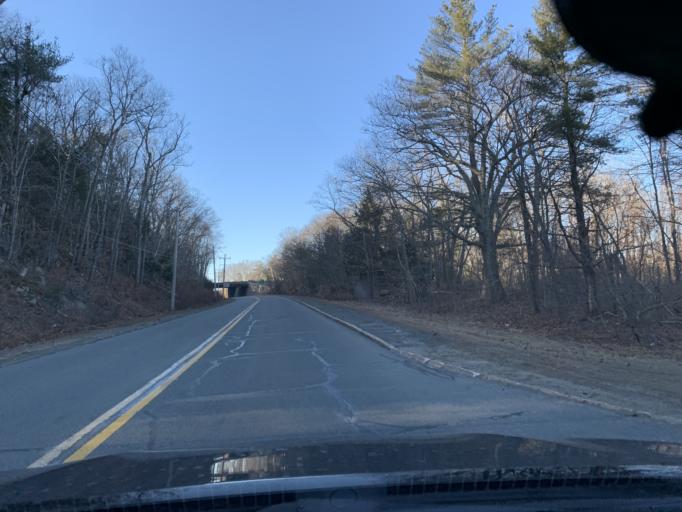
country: US
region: Massachusetts
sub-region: Essex County
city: Essex
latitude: 42.5892
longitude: -70.7907
